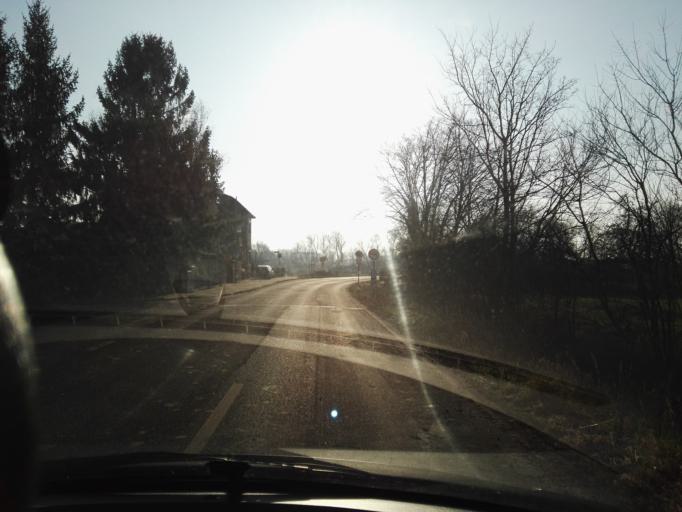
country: DE
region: Lower Saxony
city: Sarstedt
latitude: 52.2576
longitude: 9.8464
